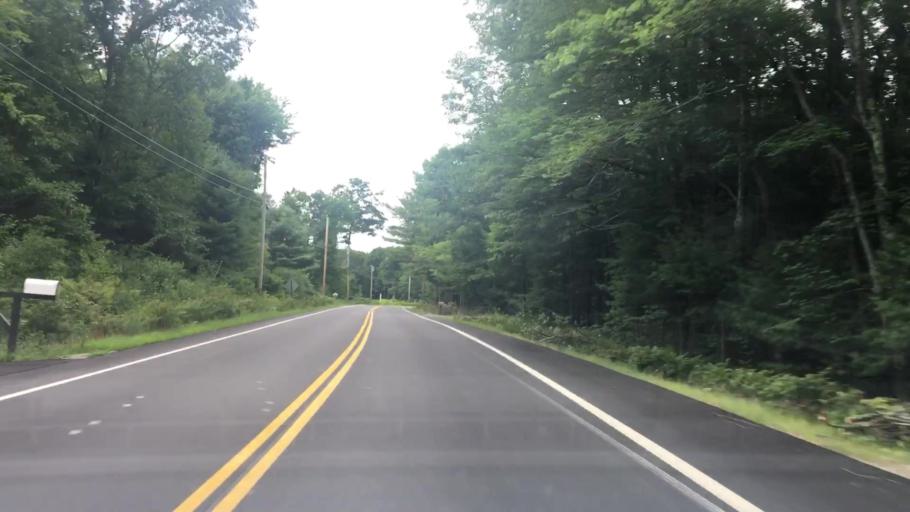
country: US
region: Maine
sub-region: York County
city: West Kennebunk
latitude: 43.4737
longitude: -70.6017
